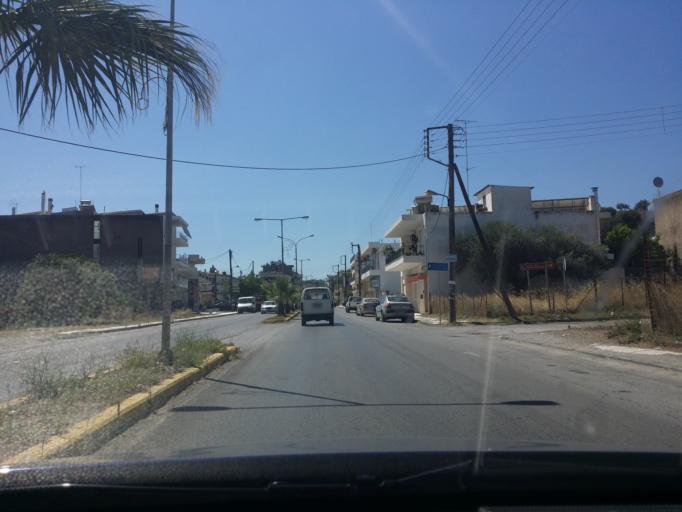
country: GR
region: Peloponnese
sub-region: Nomos Lakonias
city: Sparti
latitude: 37.0845
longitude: 22.4313
